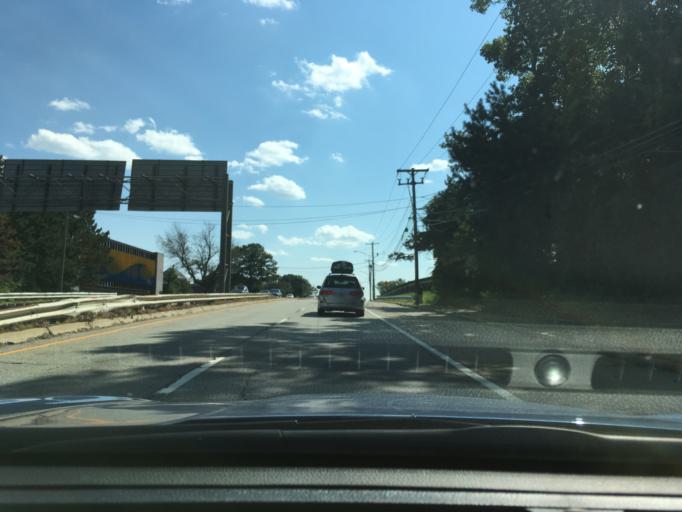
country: US
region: Rhode Island
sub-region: Providence County
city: Cranston
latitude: 41.7503
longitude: -71.4666
